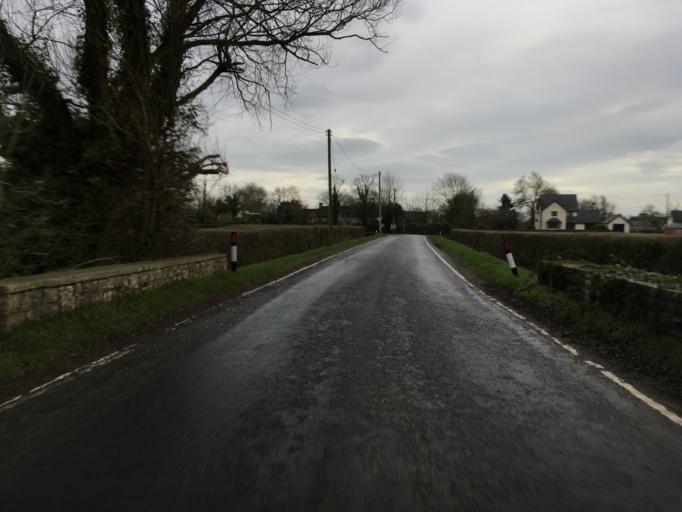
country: GB
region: Wales
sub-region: Newport
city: Redwick
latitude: 51.5568
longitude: -2.8469
